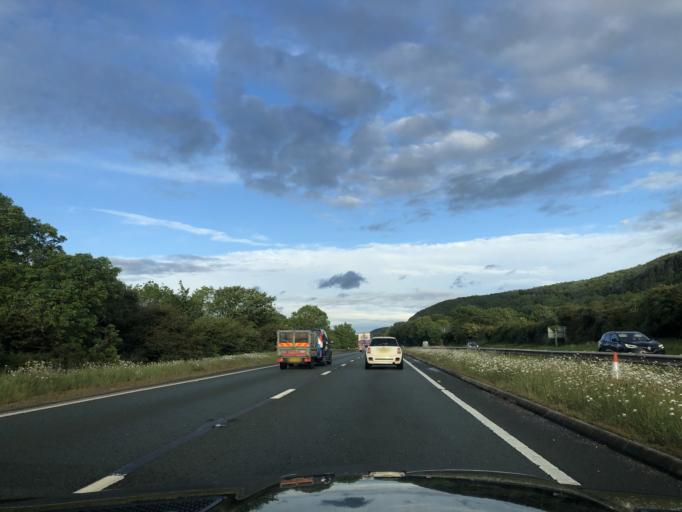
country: GB
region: Wales
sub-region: Conwy
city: Llysfaen
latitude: 53.2912
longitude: -3.6304
